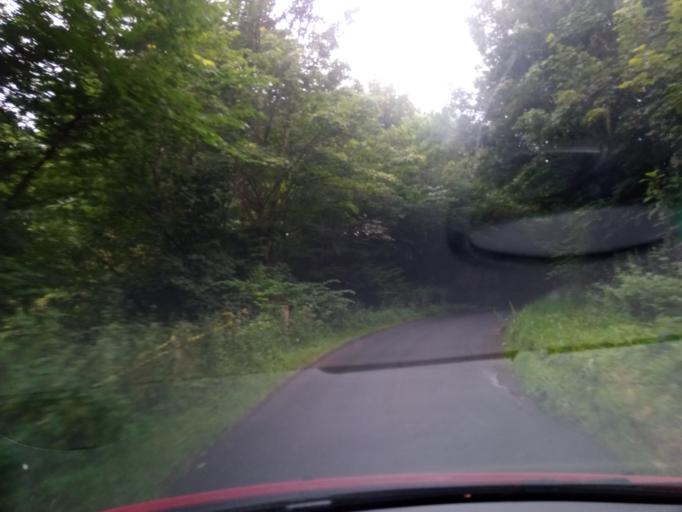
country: GB
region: Scotland
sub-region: The Scottish Borders
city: Hawick
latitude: 55.4496
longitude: -2.7693
